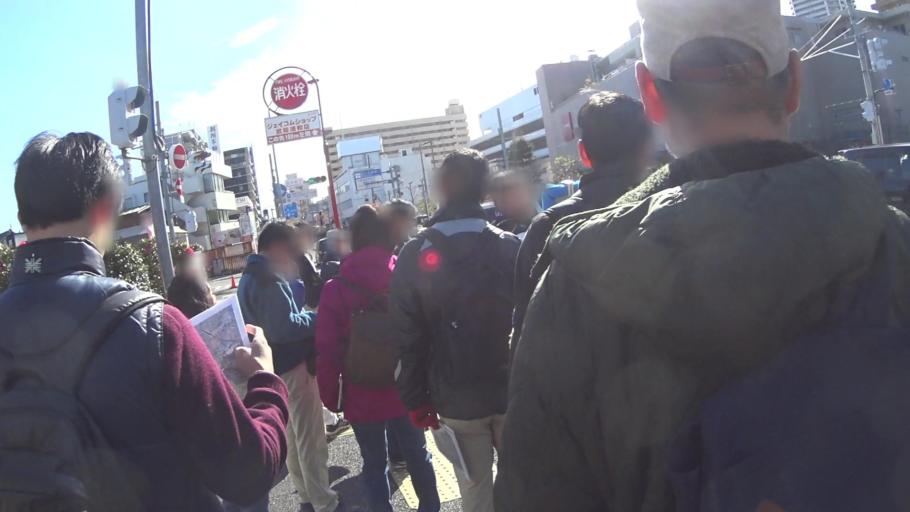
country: JP
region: Saitama
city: Yono
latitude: 35.8478
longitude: 139.6501
